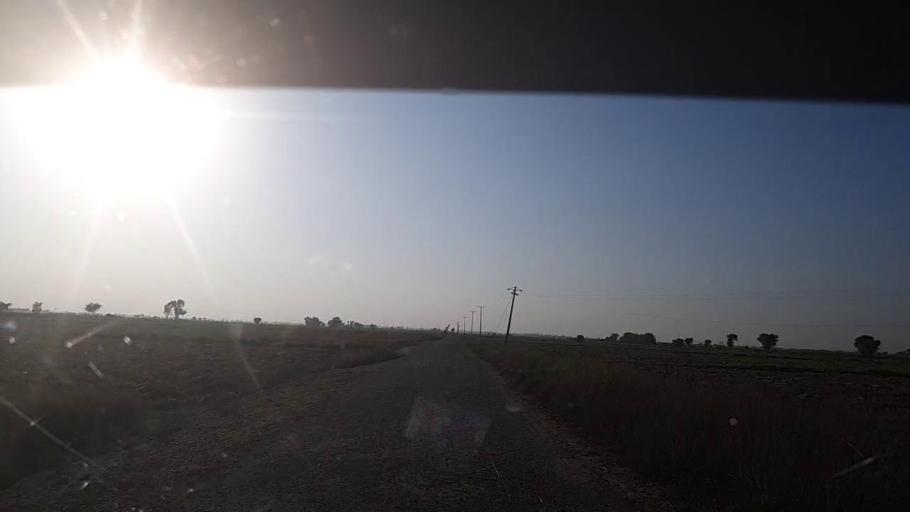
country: PK
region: Sindh
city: Ratodero
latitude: 27.8521
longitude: 68.2240
